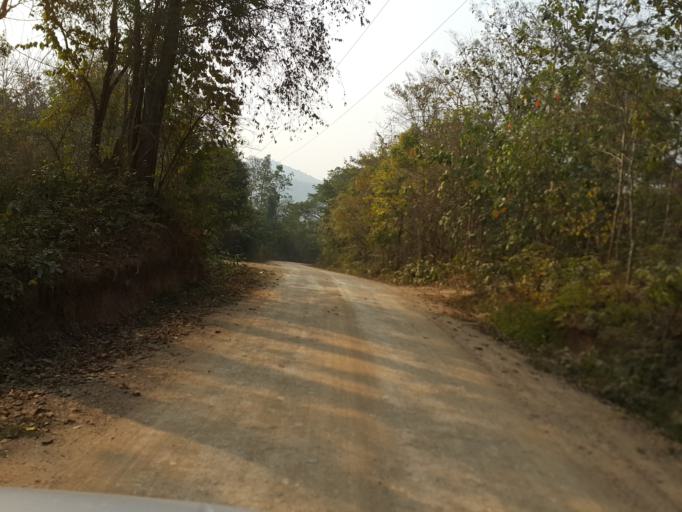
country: TH
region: Lampang
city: Mae Phrik
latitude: 17.5936
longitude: 98.9748
